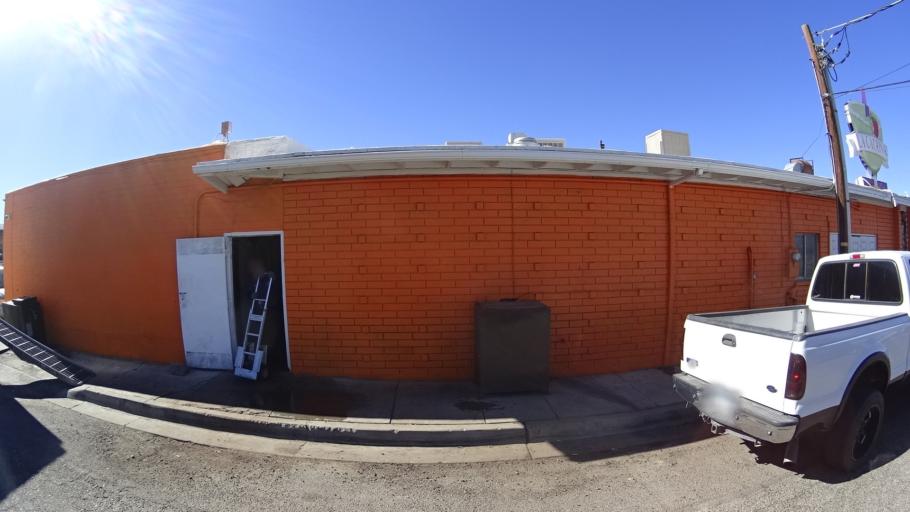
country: US
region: Arizona
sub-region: Mohave County
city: Kingman
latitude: 35.2114
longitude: -114.0155
